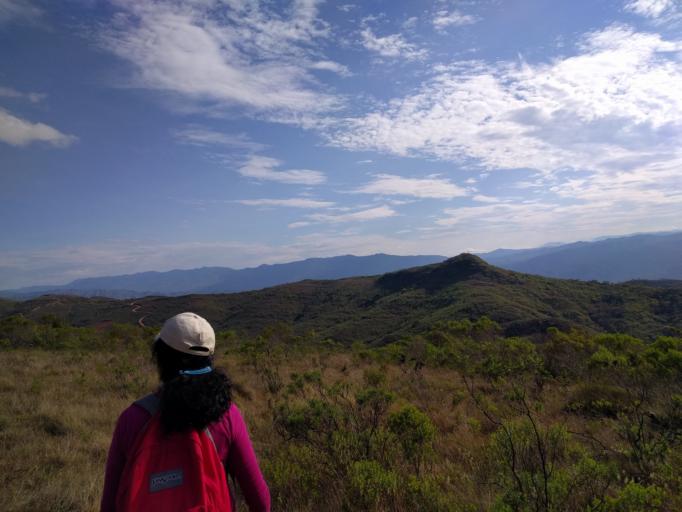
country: BO
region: Santa Cruz
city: Samaipata
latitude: -18.1867
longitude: -63.8913
